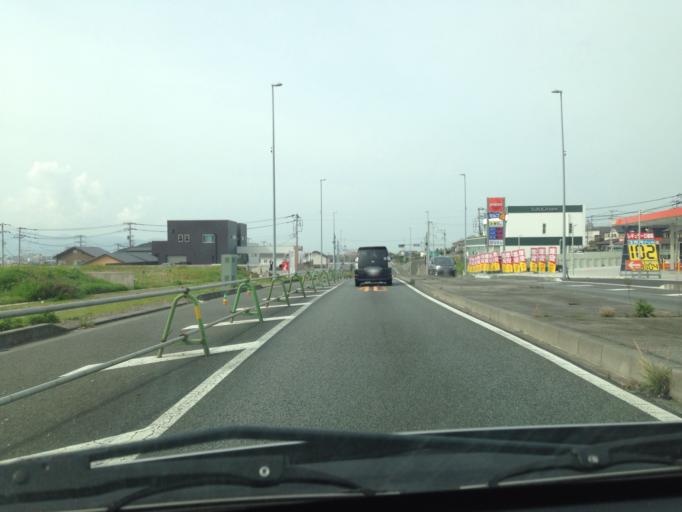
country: JP
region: Shizuoka
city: Numazu
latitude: 35.1306
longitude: 138.8719
